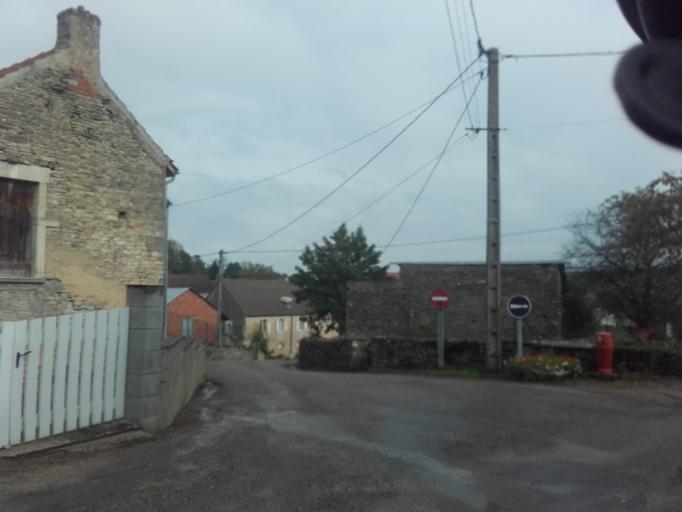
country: FR
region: Bourgogne
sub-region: Departement de la Cote-d'Or
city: Savigny-les-Beaune
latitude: 47.0507
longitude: 4.7715
